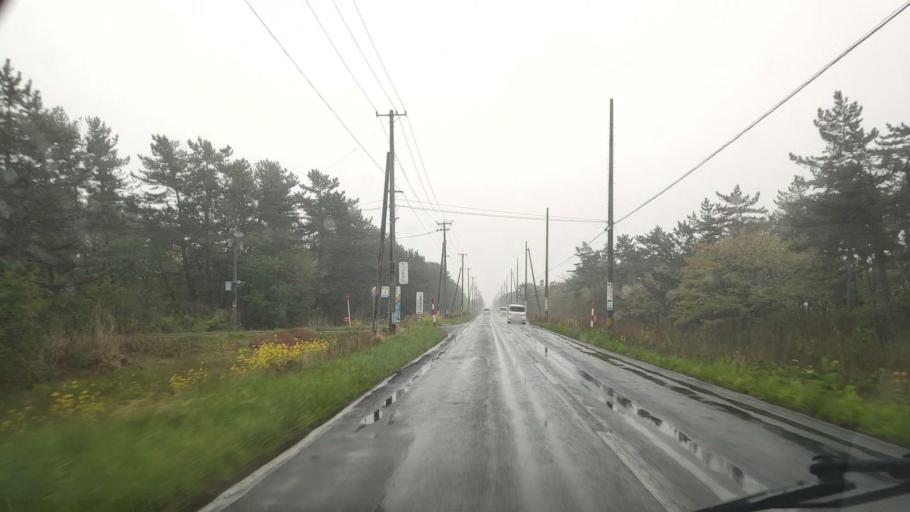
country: JP
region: Akita
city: Tenno
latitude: 40.0102
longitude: 139.9517
